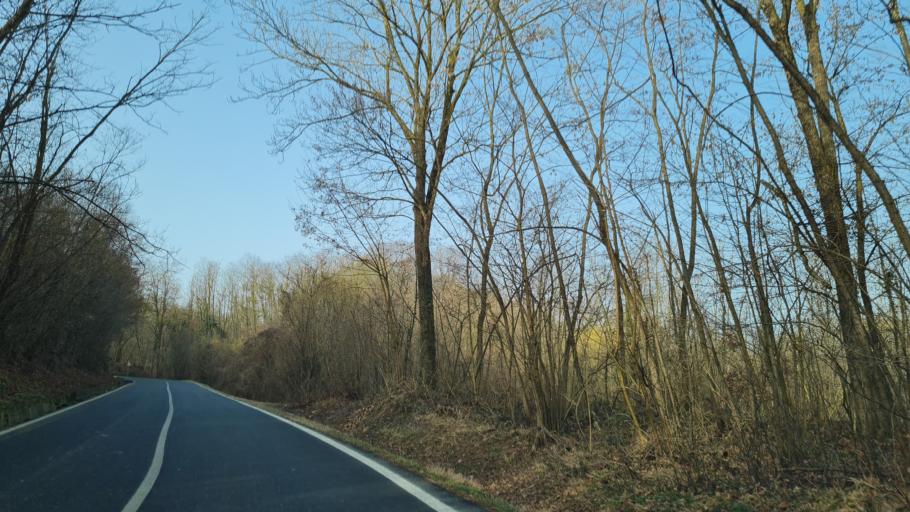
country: IT
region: Piedmont
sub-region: Provincia di Biella
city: Cerrione
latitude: 45.4648
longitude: 8.0583
